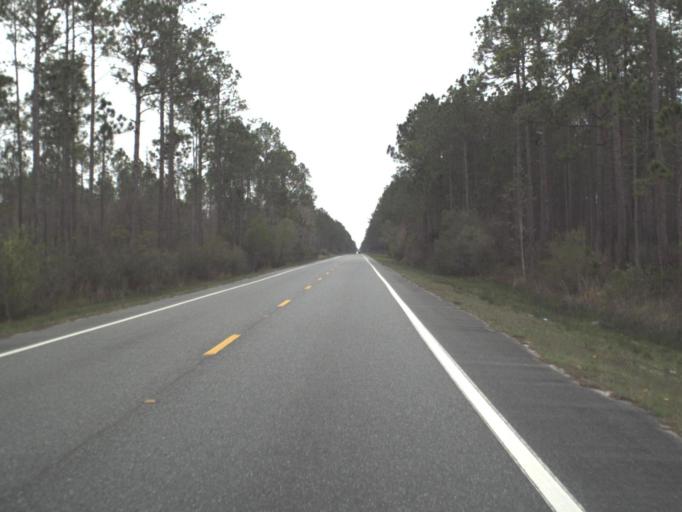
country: US
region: Florida
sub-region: Franklin County
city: Apalachicola
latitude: 29.9539
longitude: -84.9763
